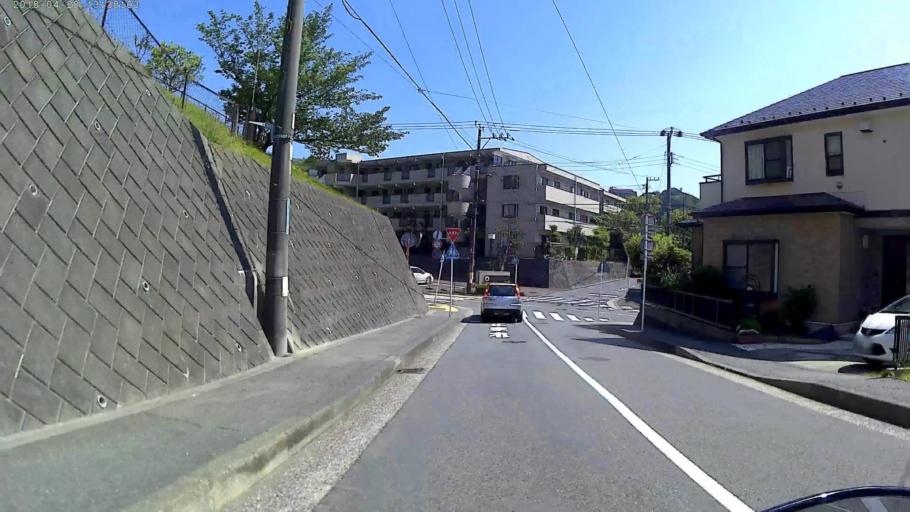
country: JP
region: Kanagawa
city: Yokosuka
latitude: 35.2155
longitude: 139.6897
